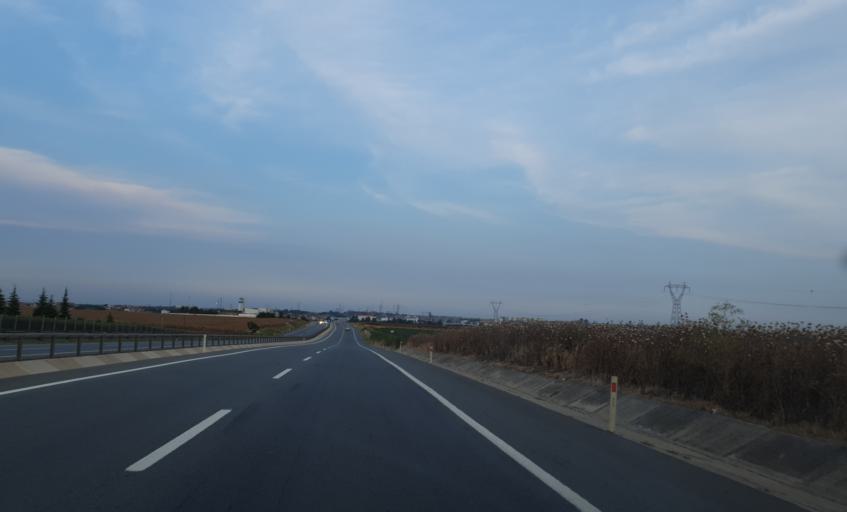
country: TR
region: Kirklareli
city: Buyukkaristiran
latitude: 41.3054
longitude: 27.5193
